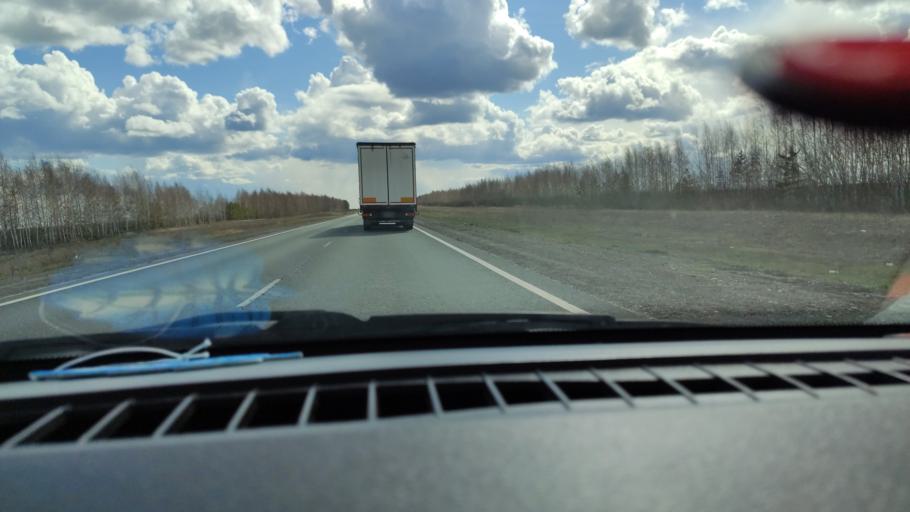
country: RU
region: Saratov
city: Dukhovnitskoye
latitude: 52.8167
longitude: 48.2320
